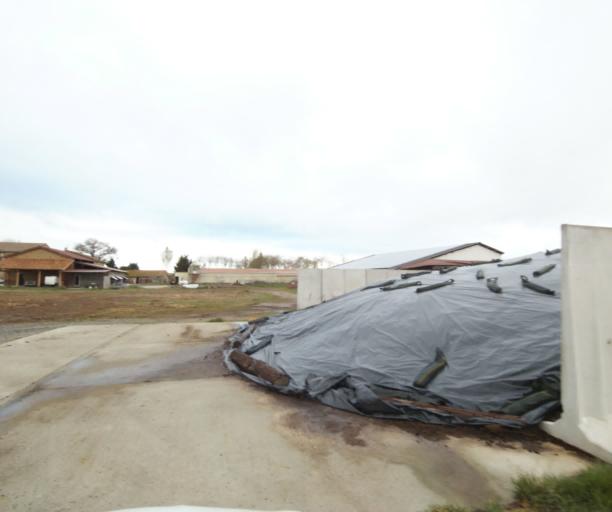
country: FR
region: Midi-Pyrenees
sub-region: Departement de la Haute-Garonne
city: Calmont
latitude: 43.2369
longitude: 1.6283
